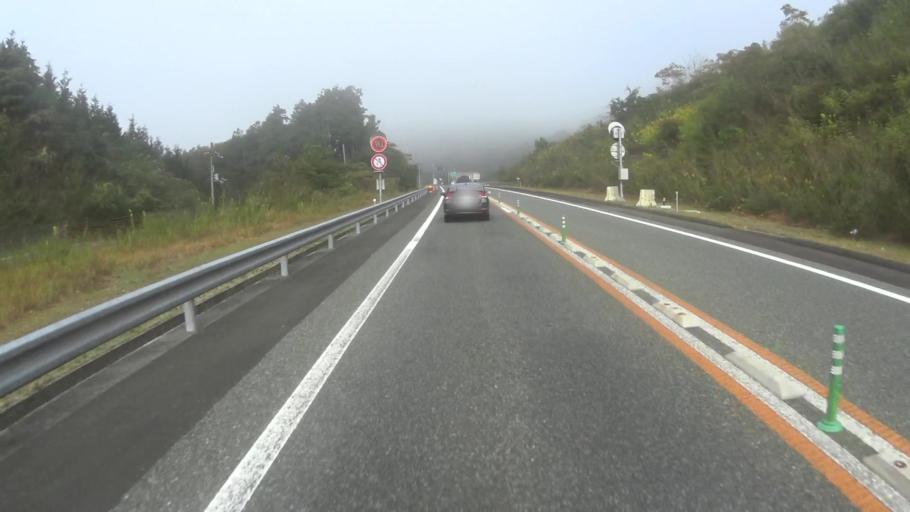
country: JP
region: Kyoto
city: Ayabe
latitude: 35.3424
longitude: 135.3024
